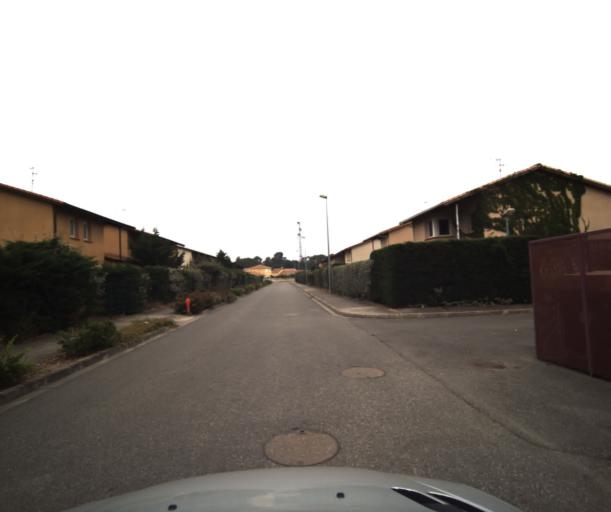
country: FR
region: Midi-Pyrenees
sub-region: Departement de la Haute-Garonne
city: Portet-sur-Garonne
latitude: 43.5346
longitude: 1.4153
